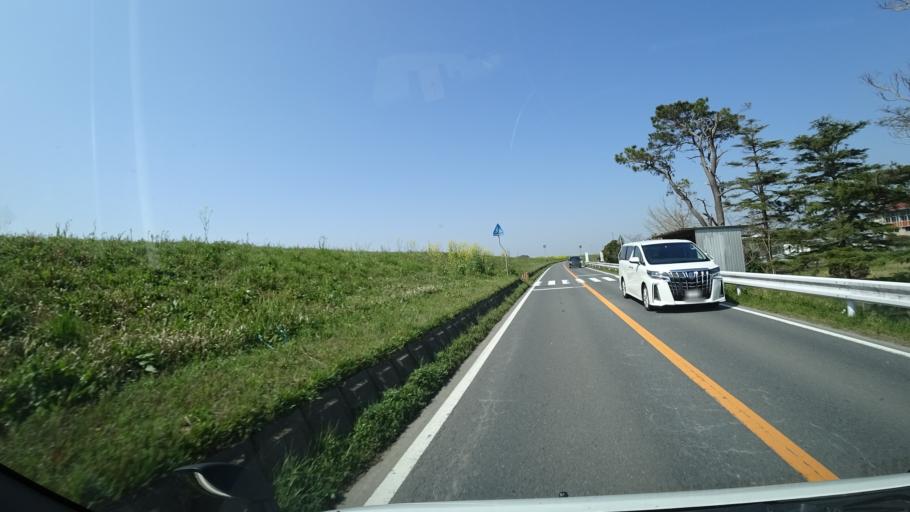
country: JP
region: Chiba
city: Katori-shi
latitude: 35.9099
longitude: 140.4224
